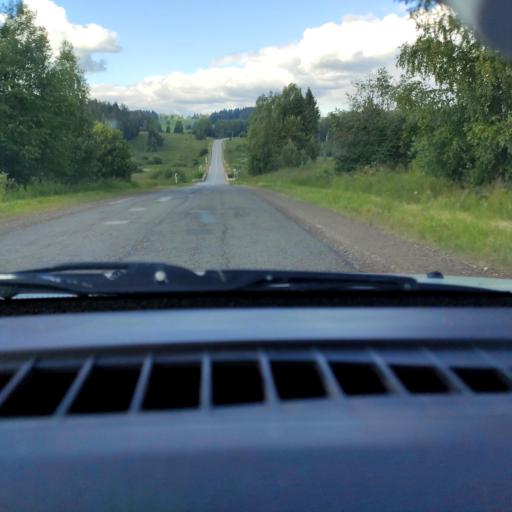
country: RU
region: Perm
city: Kukushtan
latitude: 57.3026
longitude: 56.5379
